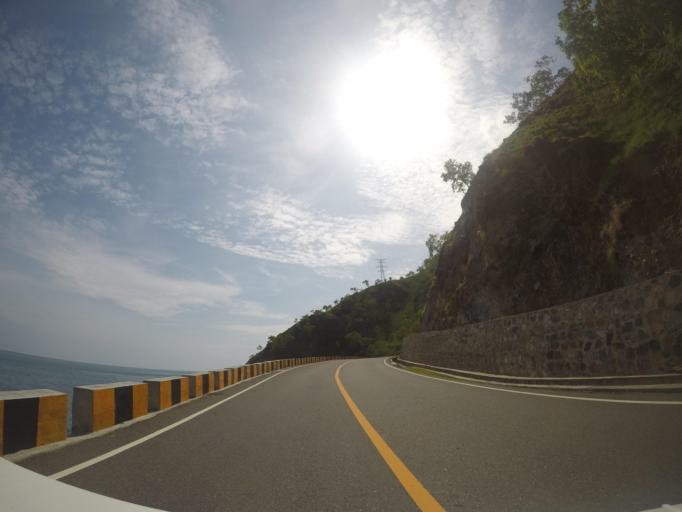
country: TL
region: Manatuto
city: Manatuto
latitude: -8.4793
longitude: 125.9293
